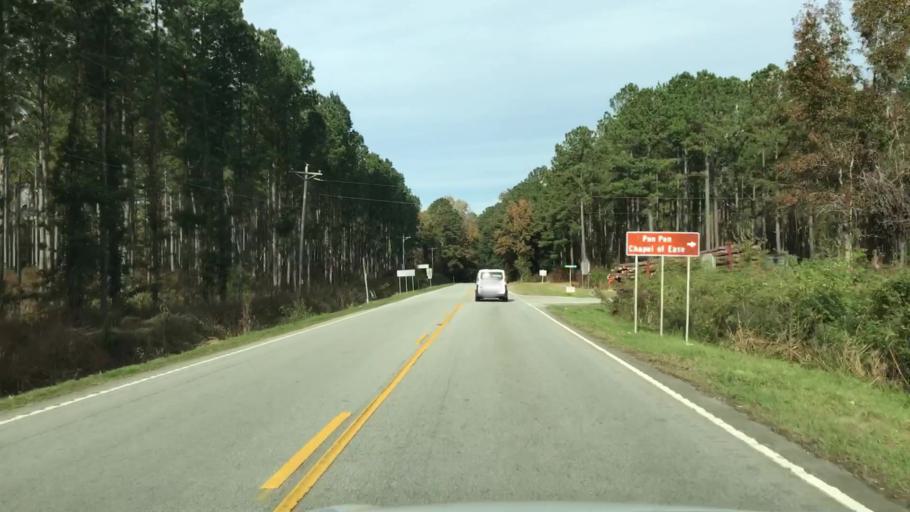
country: US
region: South Carolina
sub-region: Colleton County
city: Walterboro
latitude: 32.7949
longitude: -80.4870
